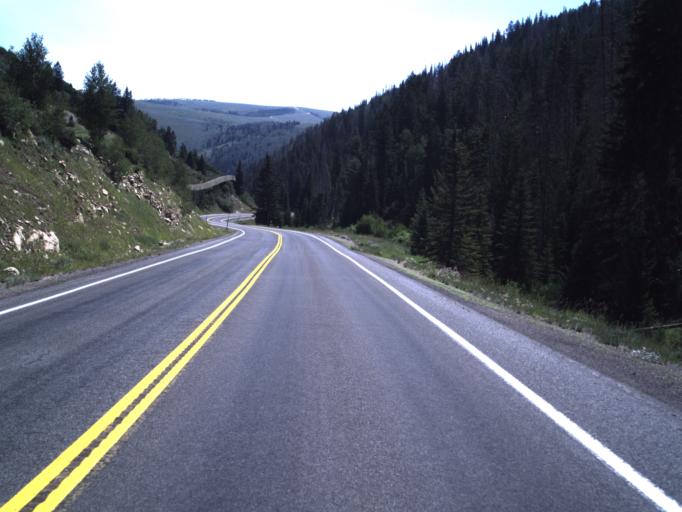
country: US
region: Utah
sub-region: Sanpete County
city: Fairview
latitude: 39.6819
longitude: -111.1806
